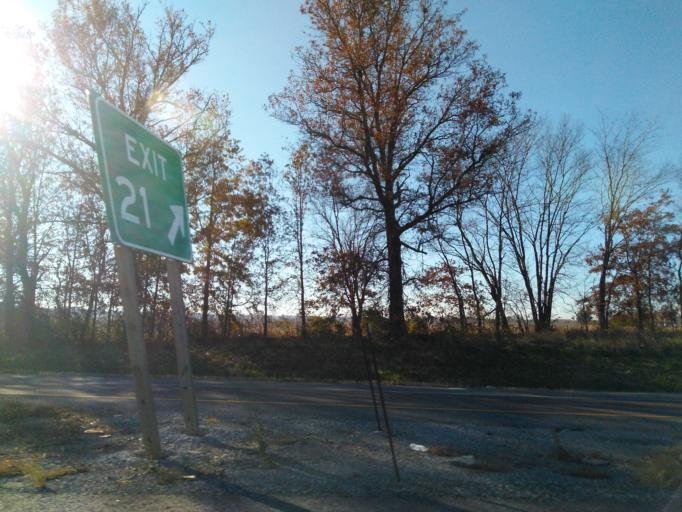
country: US
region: Illinois
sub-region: Madison County
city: Saint Jacob
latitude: 38.7619
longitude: -89.8049
